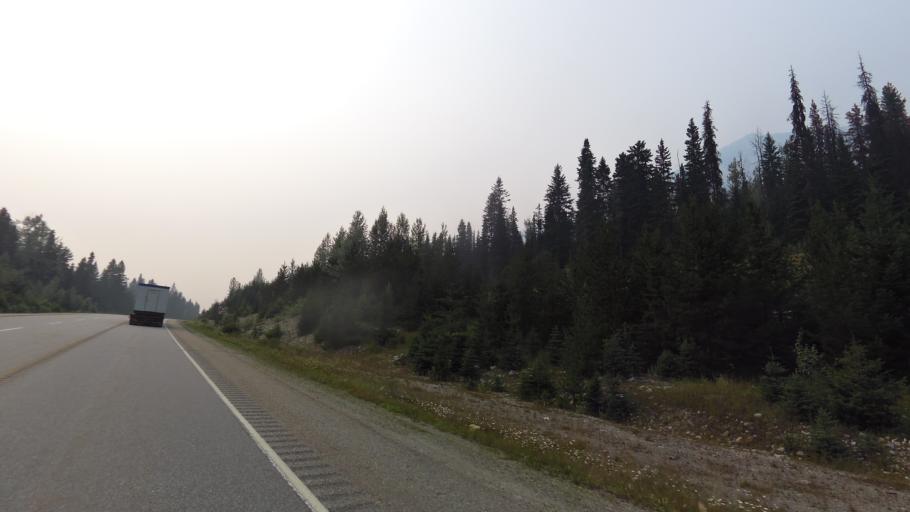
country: CA
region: Alberta
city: Grande Cache
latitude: 53.0028
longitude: -119.0438
